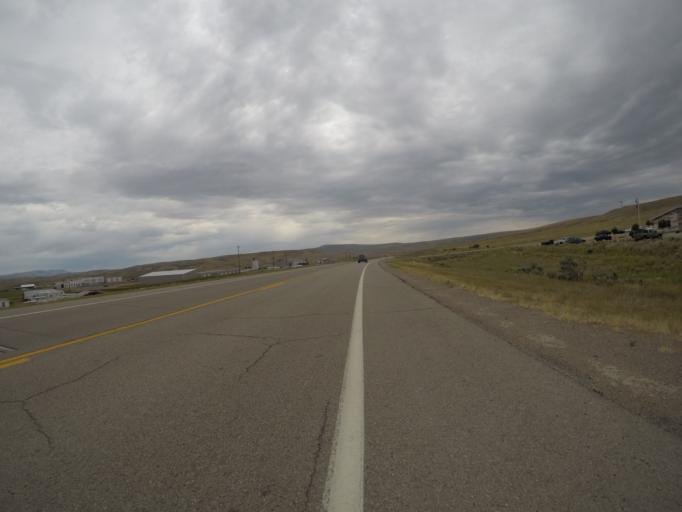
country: US
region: Wyoming
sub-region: Lincoln County
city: Kemmerer
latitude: 41.7947
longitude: -110.5740
